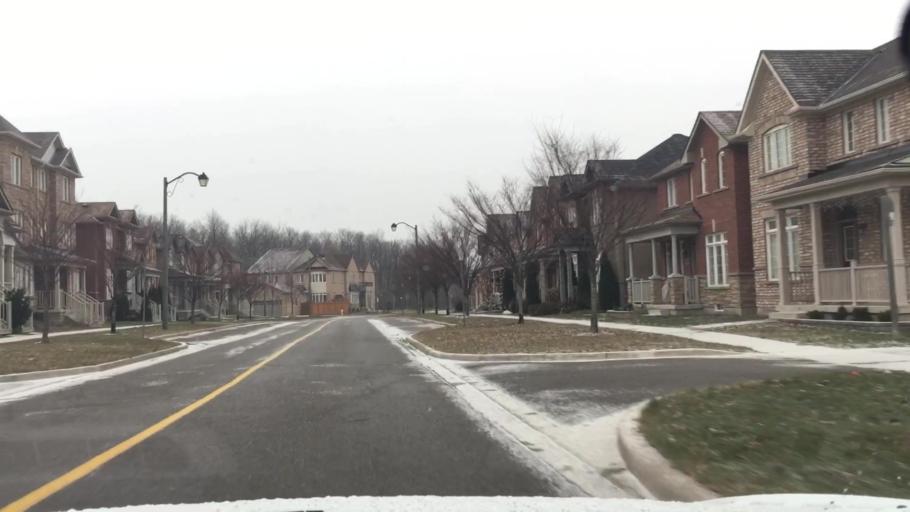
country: CA
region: Ontario
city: Markham
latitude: 43.8948
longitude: -79.2194
